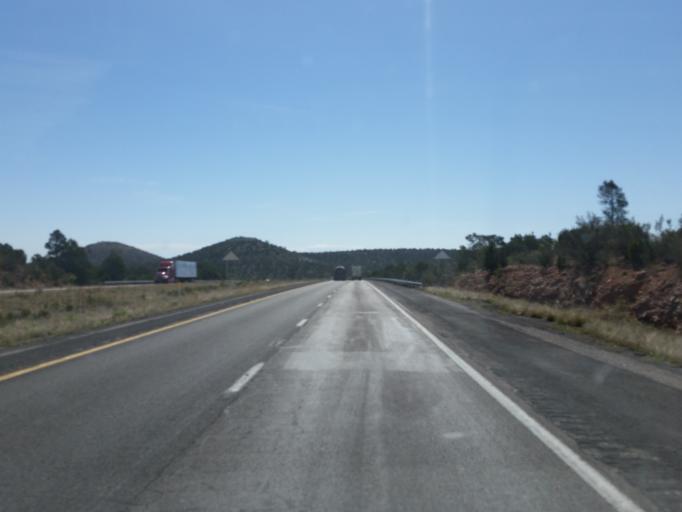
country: US
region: Arizona
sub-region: Mohave County
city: Peach Springs
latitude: 35.2921
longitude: -113.0402
